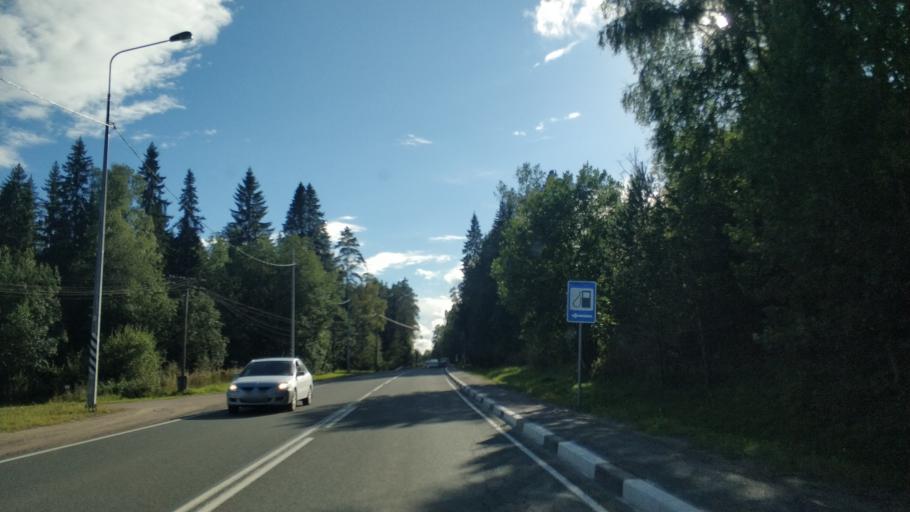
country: RU
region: Republic of Karelia
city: Lakhdenpokh'ya
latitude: 61.5342
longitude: 30.2120
